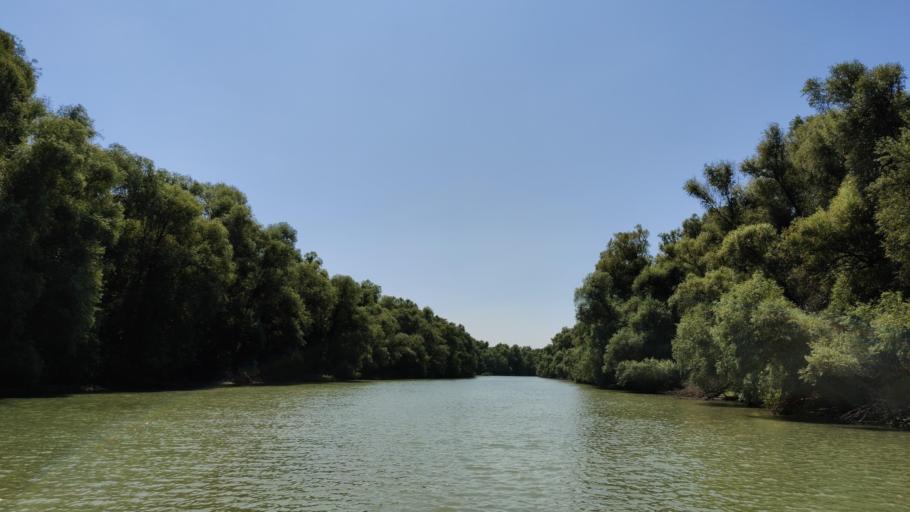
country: RO
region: Tulcea
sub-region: Comuna Pardina
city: Pardina
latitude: 45.2402
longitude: 28.9191
